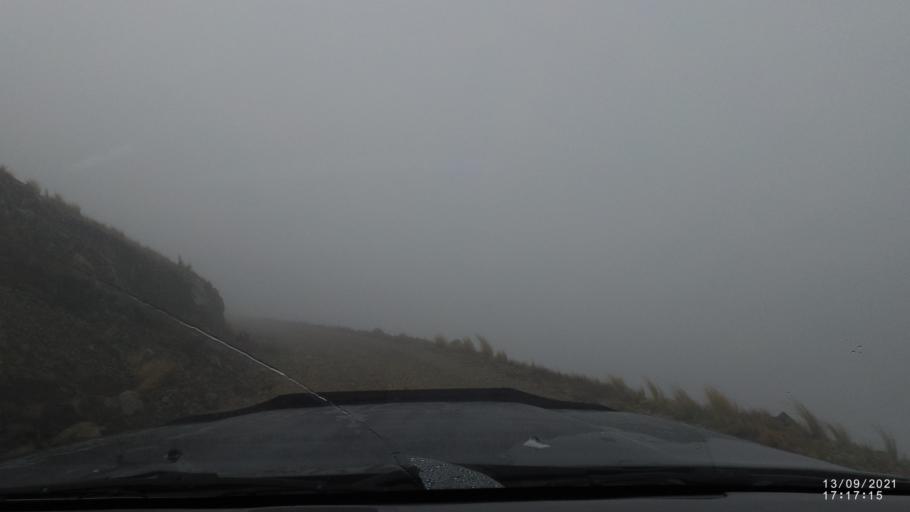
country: BO
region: Cochabamba
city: Colomi
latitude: -17.3451
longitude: -65.7599
